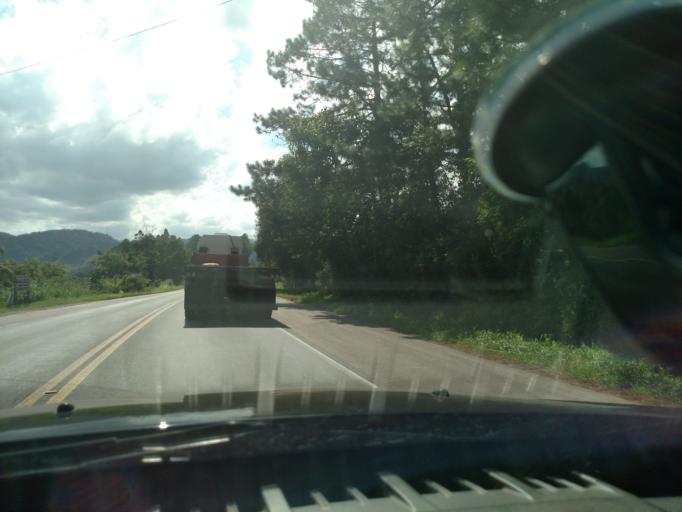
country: BR
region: Santa Catarina
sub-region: Rodeio
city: Gavea
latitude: -26.9515
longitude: -49.3069
